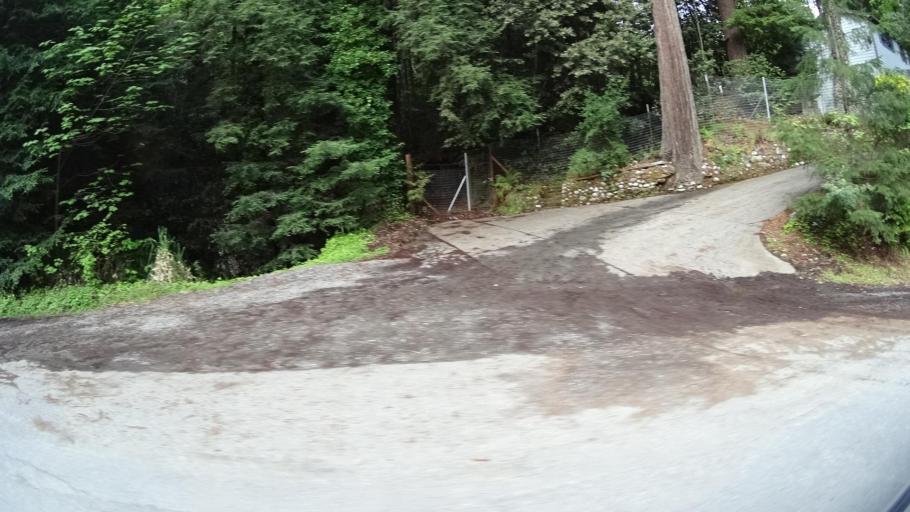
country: US
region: California
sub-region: Humboldt County
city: Redway
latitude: 40.3362
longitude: -123.9097
